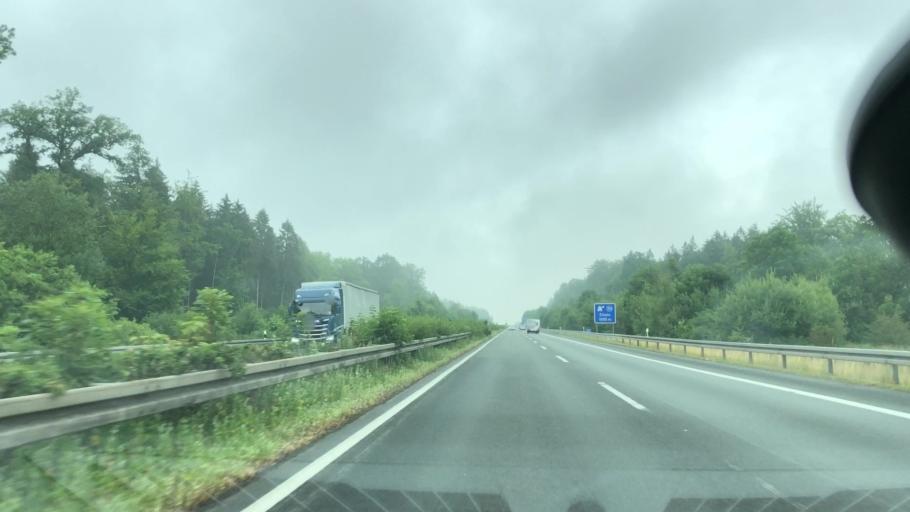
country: DE
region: North Rhine-Westphalia
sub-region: Regierungsbezirk Detmold
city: Wunnenberg
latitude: 51.6006
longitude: 8.7307
